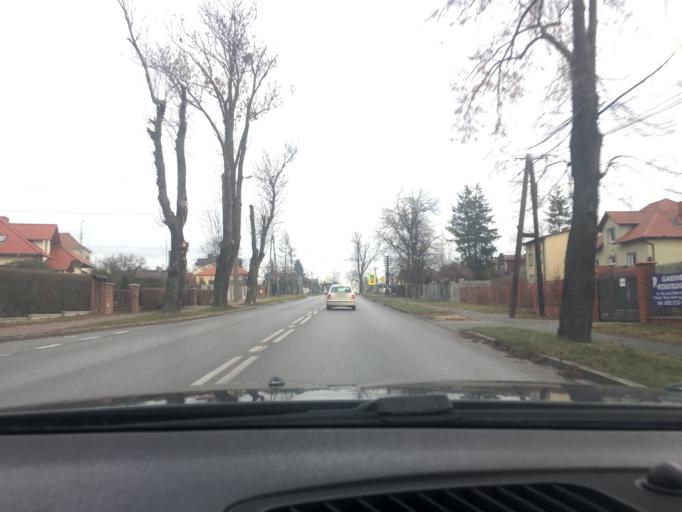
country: PL
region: Swietokrzyskie
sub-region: Powiat jedrzejowski
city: Jedrzejow
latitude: 50.6417
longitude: 20.3082
